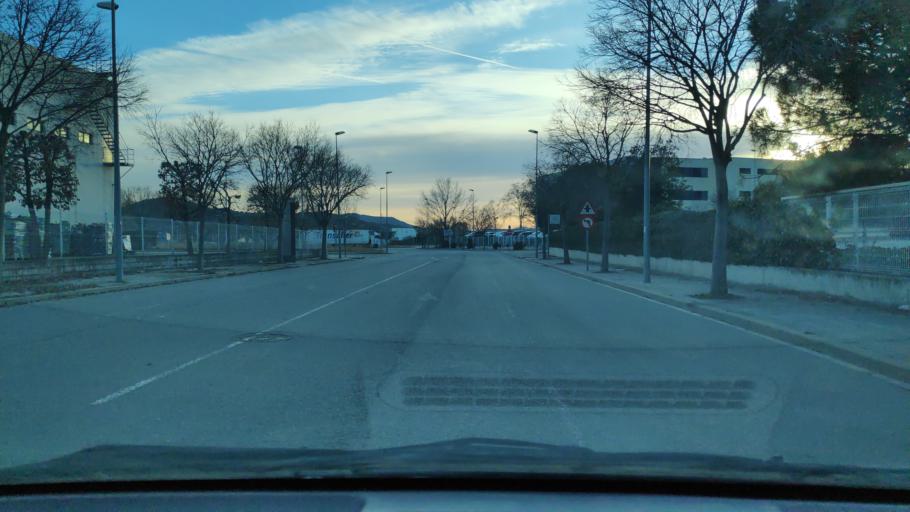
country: ES
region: Catalonia
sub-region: Provincia de Barcelona
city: Montmelo
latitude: 41.5673
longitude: 2.2645
